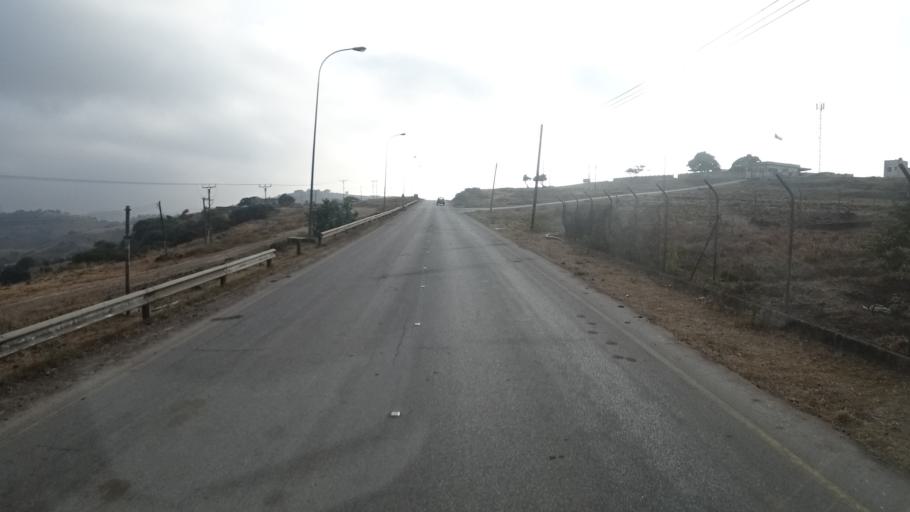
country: OM
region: Zufar
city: Salalah
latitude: 17.1252
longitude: 53.9956
